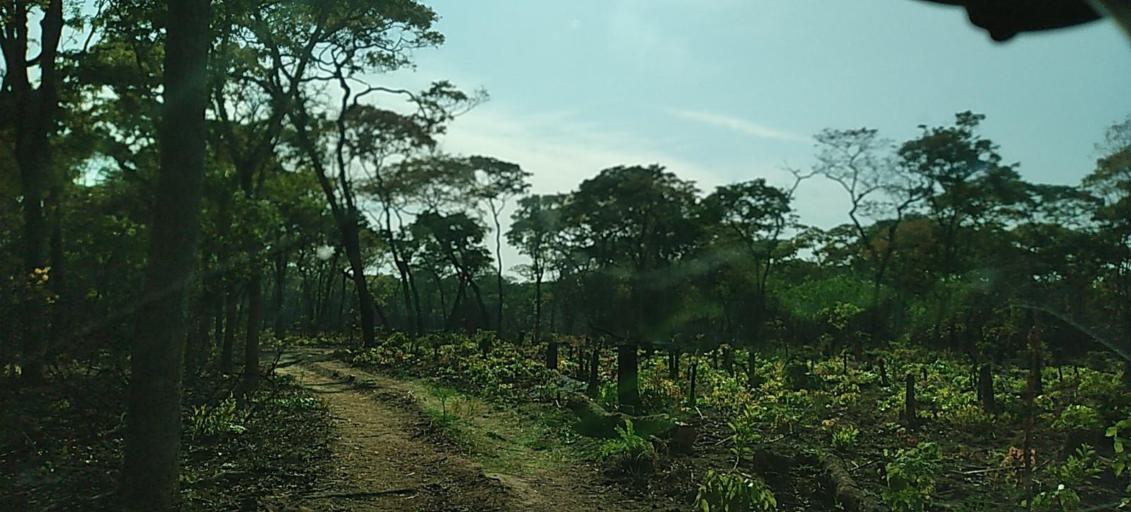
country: ZM
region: North-Western
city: Kalengwa
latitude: -13.2337
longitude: 25.0690
